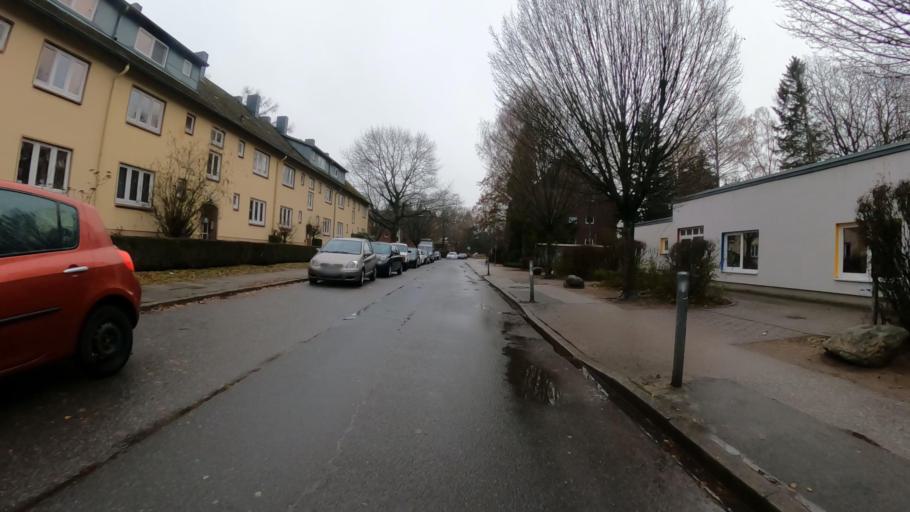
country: DE
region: Hamburg
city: Farmsen-Berne
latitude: 53.6168
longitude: 10.1539
